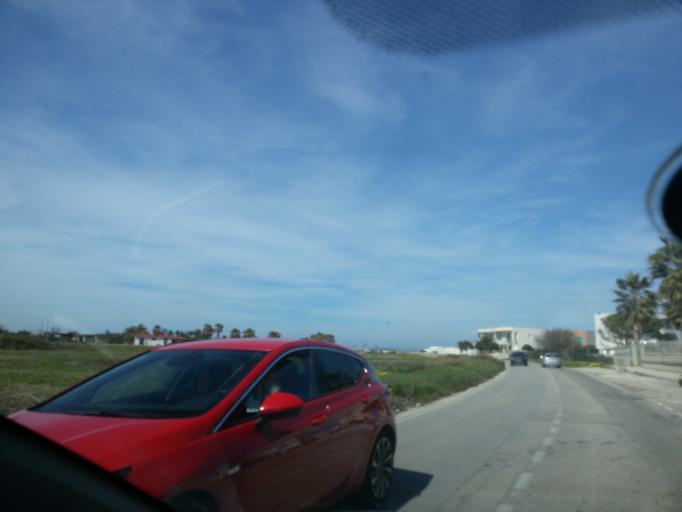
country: IT
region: Apulia
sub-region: Provincia di Brindisi
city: Pezze di Greco
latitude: 40.8418
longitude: 17.4648
